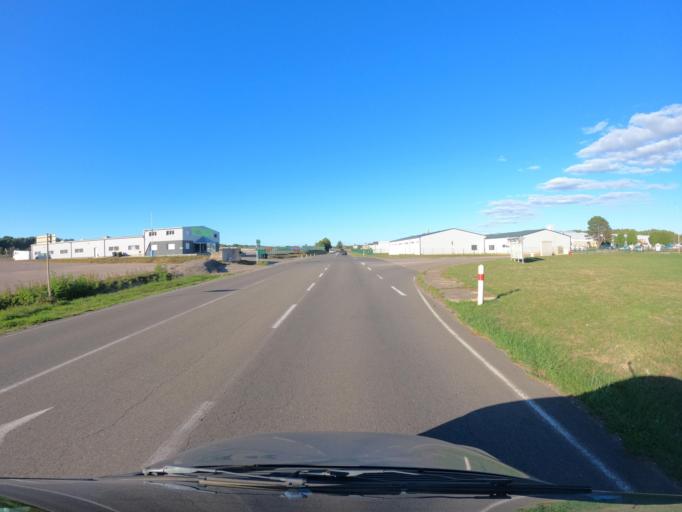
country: FR
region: Bourgogne
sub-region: Departement de Saone-et-Loire
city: Torcy
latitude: 46.7617
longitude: 4.4428
